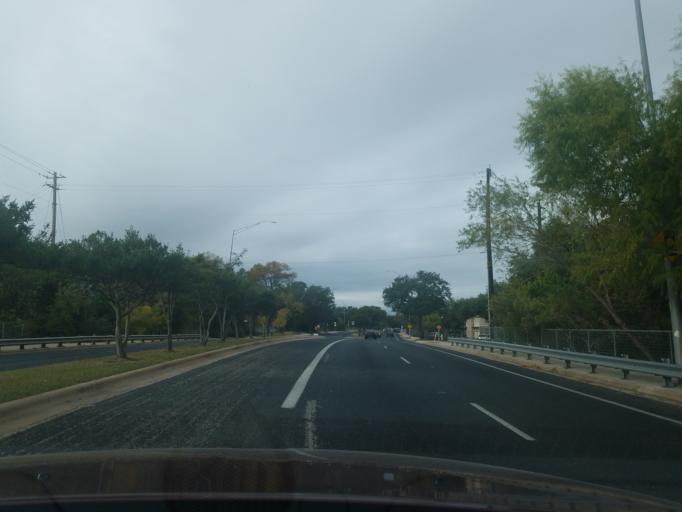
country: US
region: Texas
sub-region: Williamson County
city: Anderson Mill
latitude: 30.4763
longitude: -97.8083
